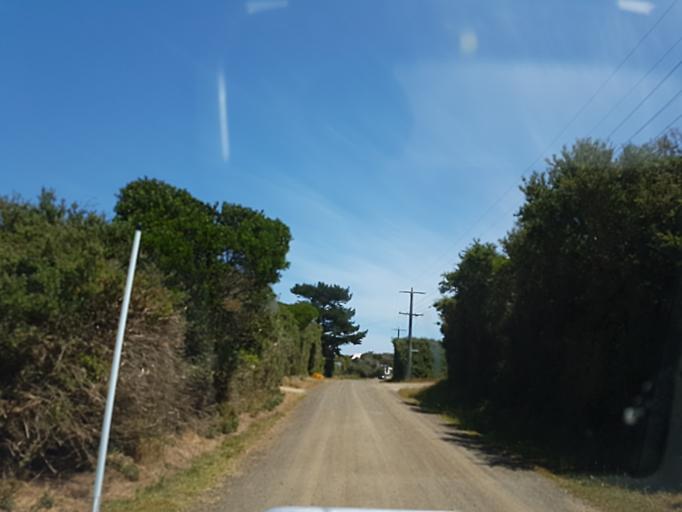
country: AU
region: Victoria
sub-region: Bass Coast
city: North Wonthaggi
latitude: -38.6997
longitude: 145.8255
